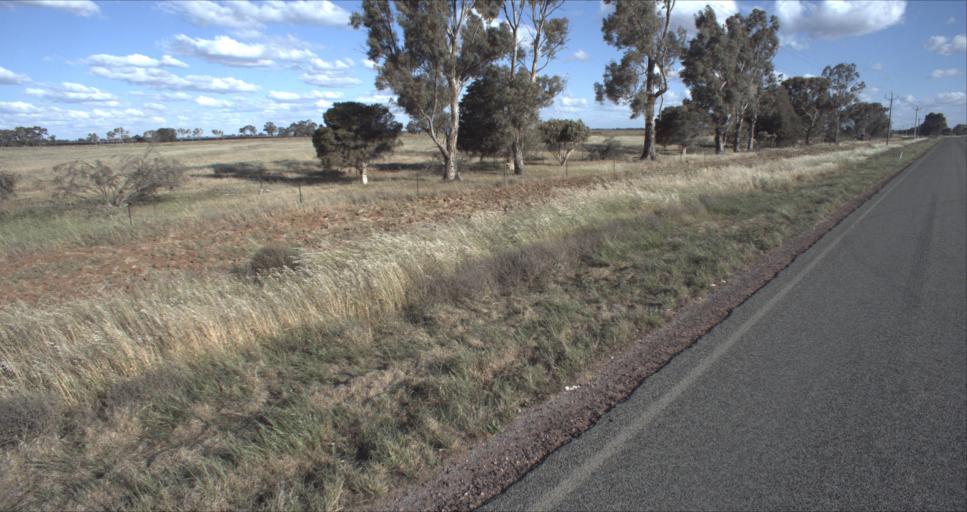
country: AU
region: New South Wales
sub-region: Leeton
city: Leeton
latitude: -34.5348
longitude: 146.2808
